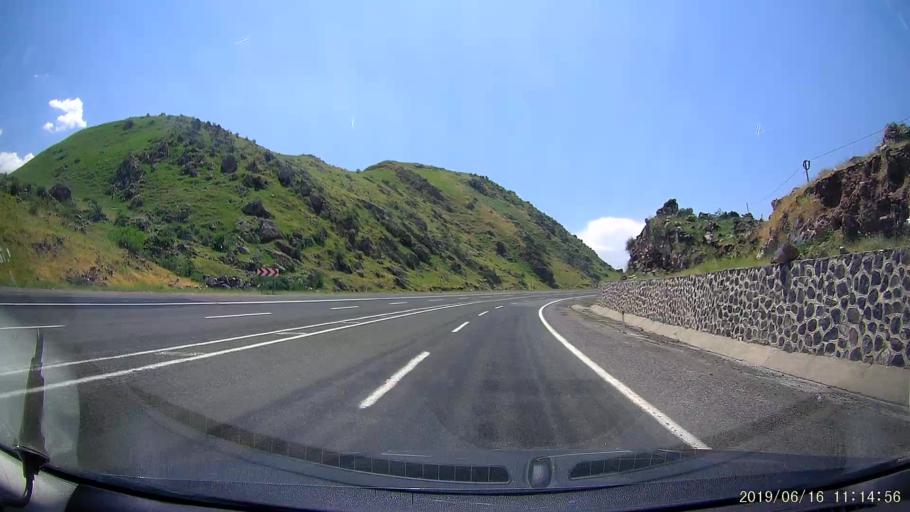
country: TR
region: Igdir
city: Igdir
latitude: 39.7713
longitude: 44.1434
